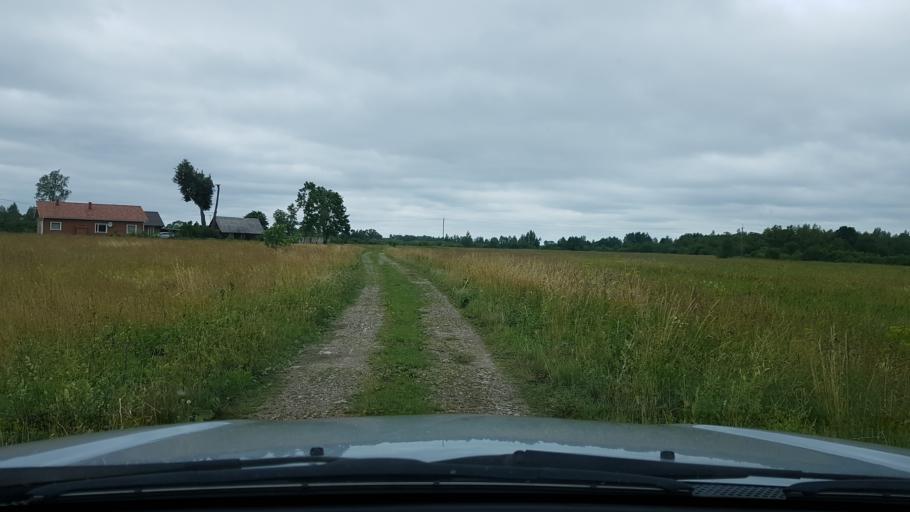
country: EE
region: Ida-Virumaa
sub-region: Narva linn
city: Narva
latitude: 59.3786
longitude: 28.1210
